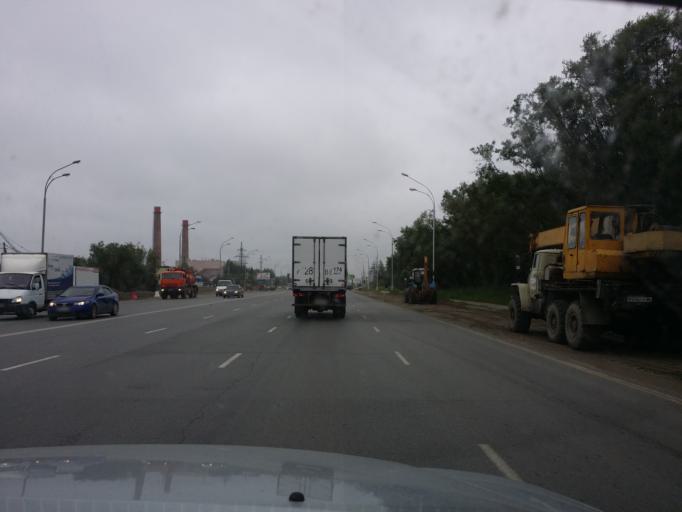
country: RU
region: Khanty-Mansiyskiy Avtonomnyy Okrug
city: Nizhnevartovsk
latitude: 60.9427
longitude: 76.5301
